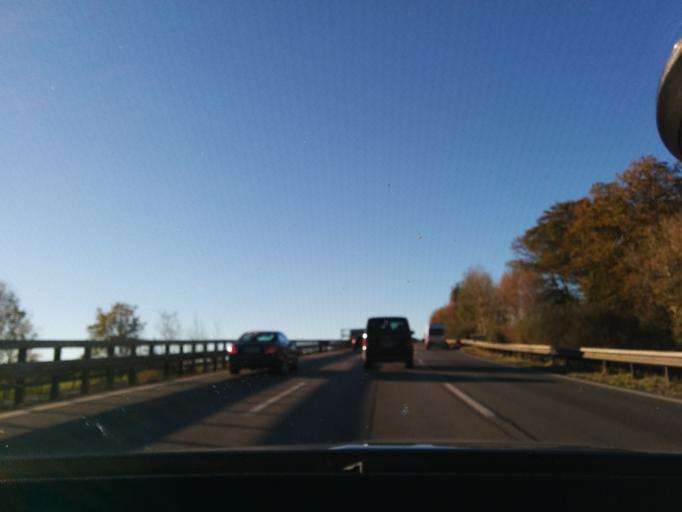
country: DE
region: Bavaria
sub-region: Upper Bavaria
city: Irschenberg
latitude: 47.8234
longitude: 11.9250
